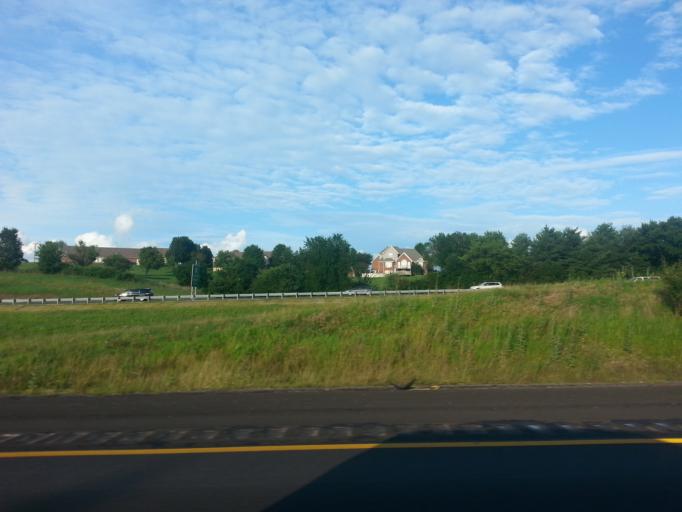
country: US
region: Kentucky
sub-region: Madison County
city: Richmond
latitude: 37.7180
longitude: -84.3218
